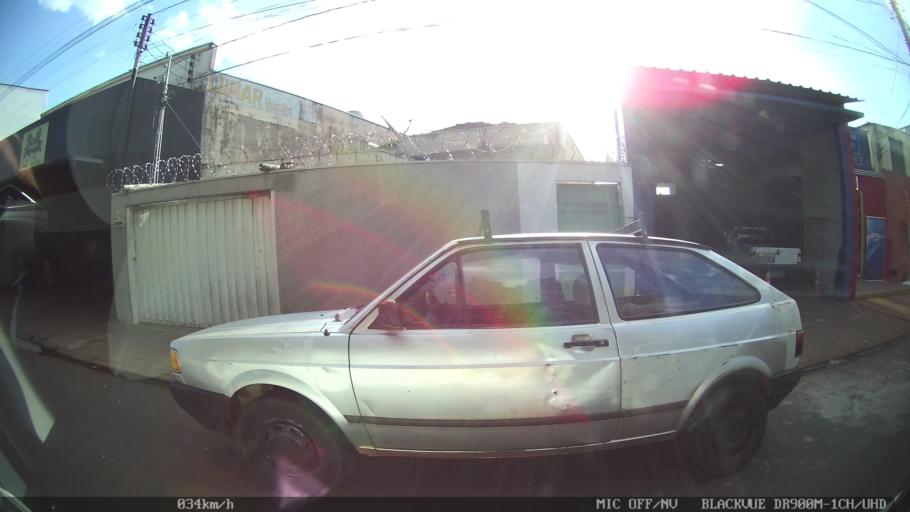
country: BR
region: Sao Paulo
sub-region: Ribeirao Preto
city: Ribeirao Preto
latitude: -21.1530
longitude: -47.8054
